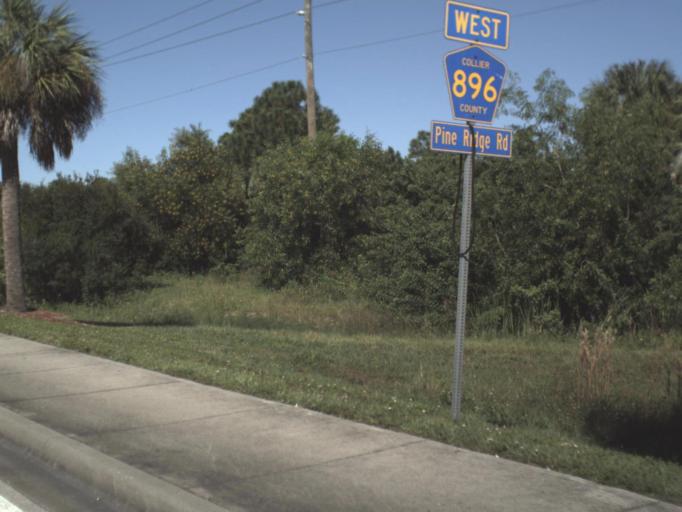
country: US
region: Florida
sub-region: Collier County
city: Vineyards
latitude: 26.2117
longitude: -81.7411
